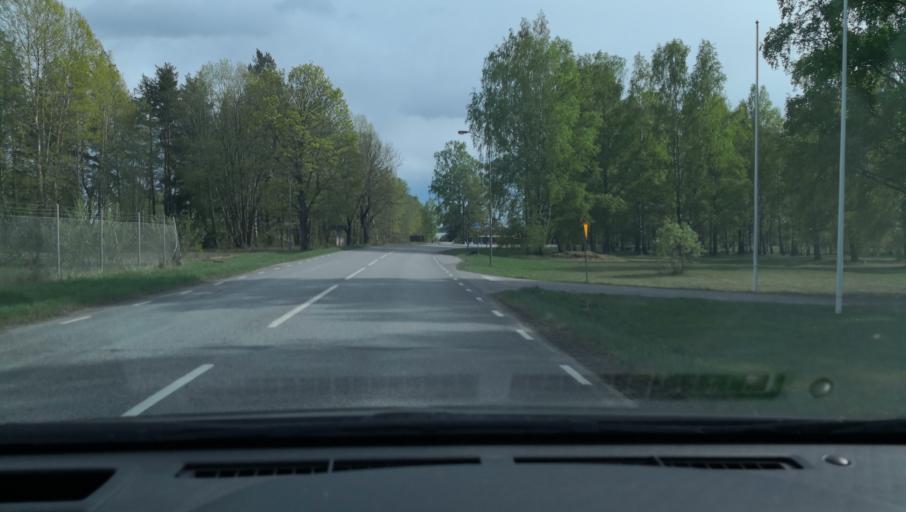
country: SE
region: OErebro
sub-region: Kumla Kommun
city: Kumla
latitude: 59.0886
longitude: 15.1590
